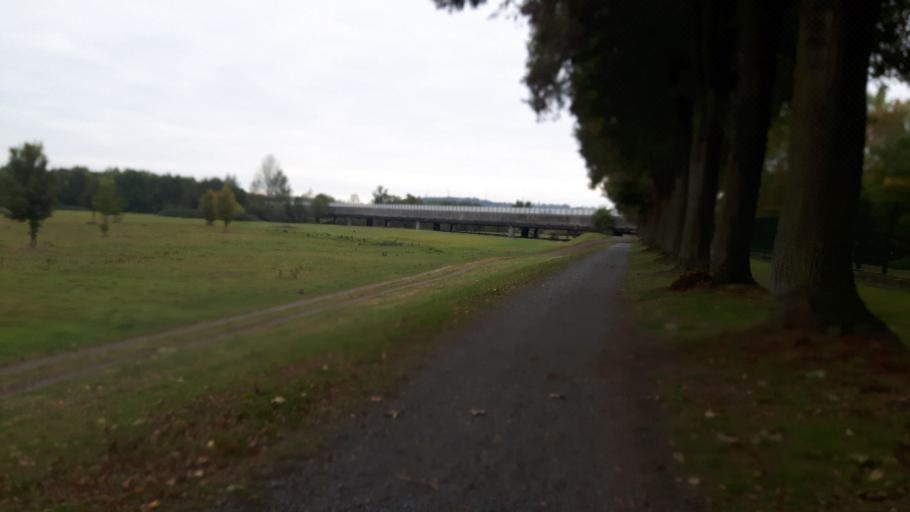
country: DE
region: North Rhine-Westphalia
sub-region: Regierungsbezirk Koln
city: Hennef
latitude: 50.7839
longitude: 7.2860
